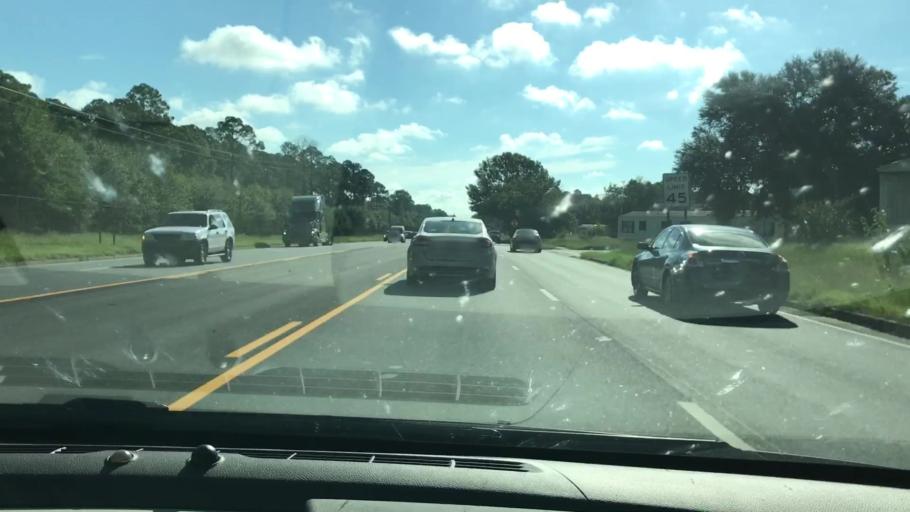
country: US
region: Georgia
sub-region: Dougherty County
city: Albany
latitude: 31.5799
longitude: -84.0983
